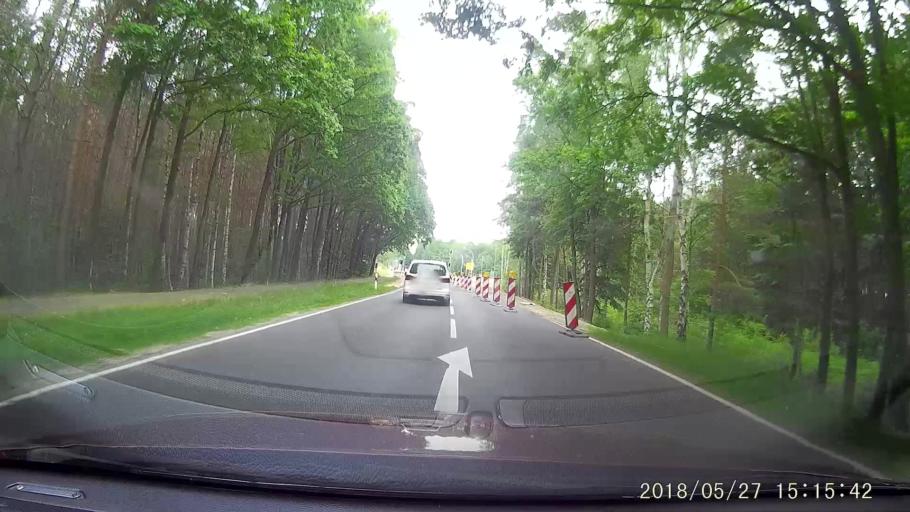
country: DE
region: Saxony
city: Niesky
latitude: 51.2801
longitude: 14.8157
